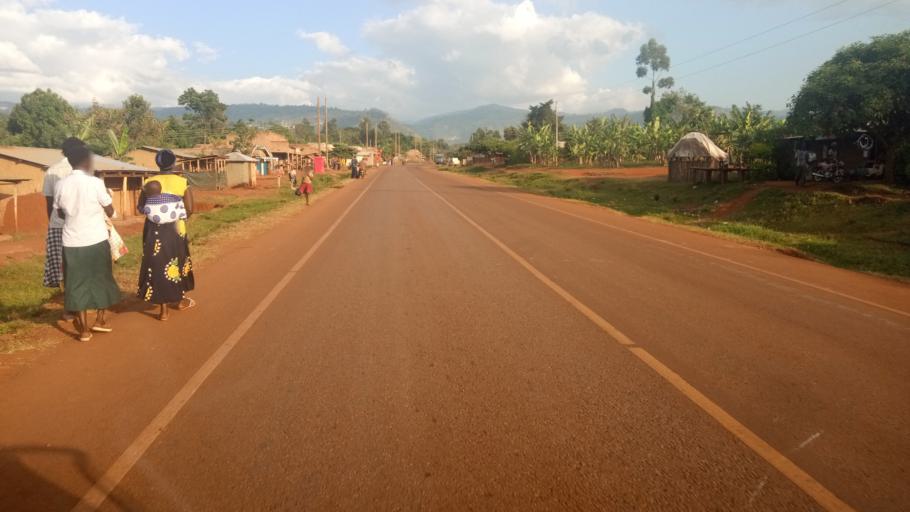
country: UG
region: Eastern Region
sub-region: Sironko District
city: Sironko
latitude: 1.3220
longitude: 34.3350
